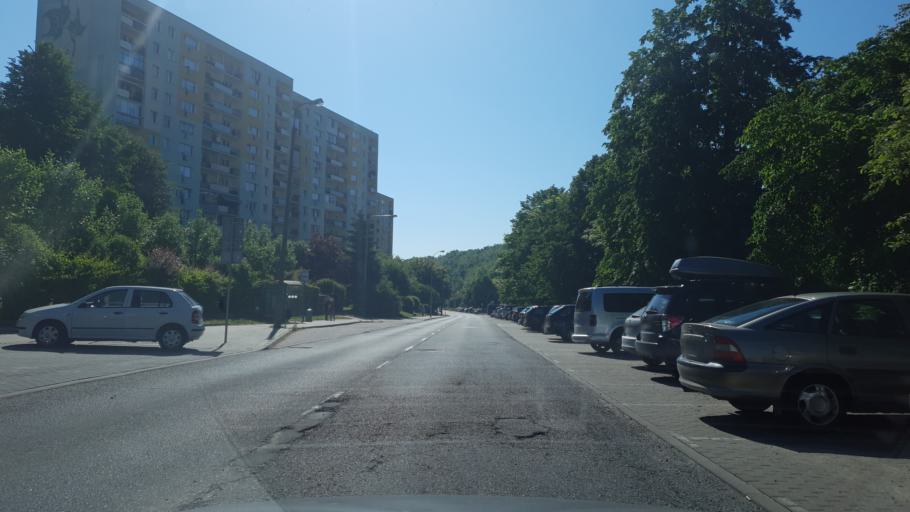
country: PL
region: Pomeranian Voivodeship
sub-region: Sopot
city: Sopot
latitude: 54.4573
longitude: 18.5373
